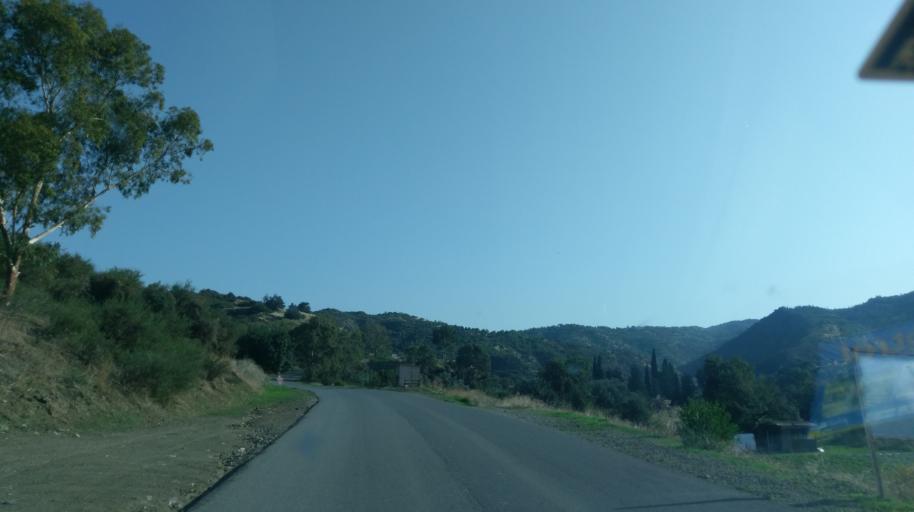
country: CY
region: Lefkosia
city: Kato Pyrgos
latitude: 35.1656
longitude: 32.7477
